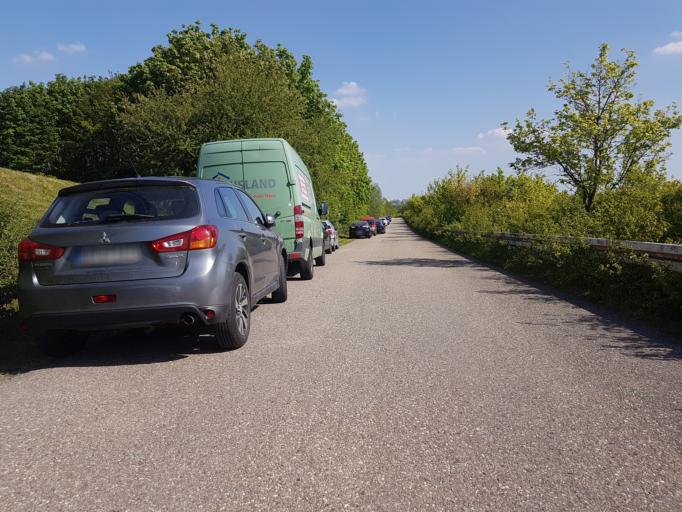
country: DE
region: Baden-Wuerttemberg
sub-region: Regierungsbezirk Stuttgart
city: Asperg
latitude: 48.9264
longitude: 9.1511
